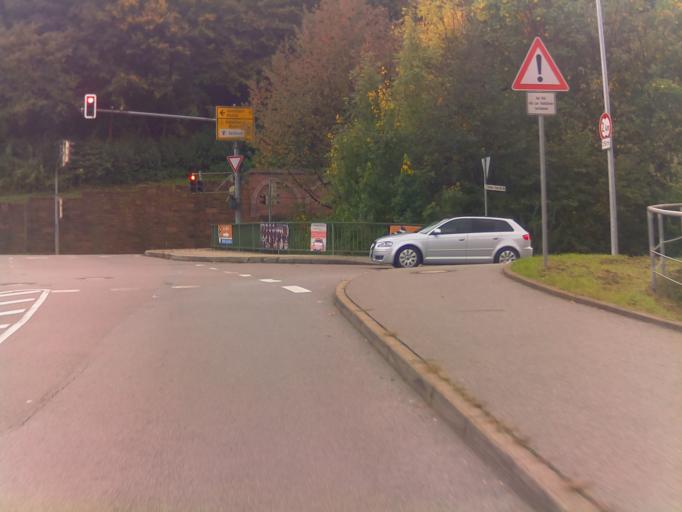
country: DE
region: Baden-Wuerttemberg
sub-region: Karlsruhe Region
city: Eberbach
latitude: 49.4722
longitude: 8.9863
